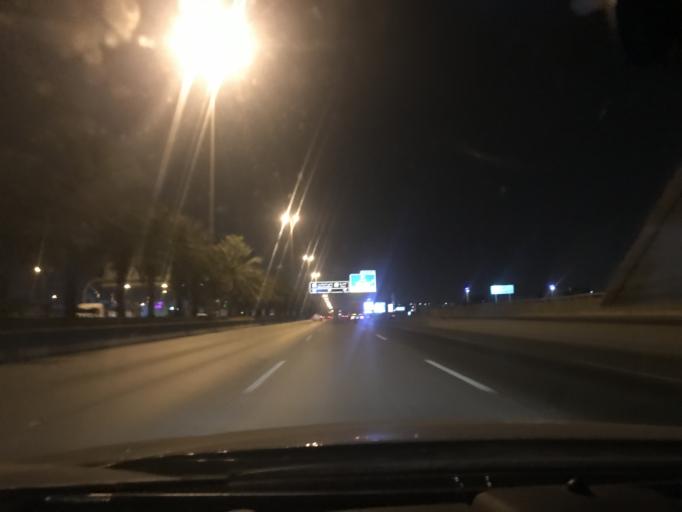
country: SA
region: Ar Riyad
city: Riyadh
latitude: 24.7688
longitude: 46.7341
